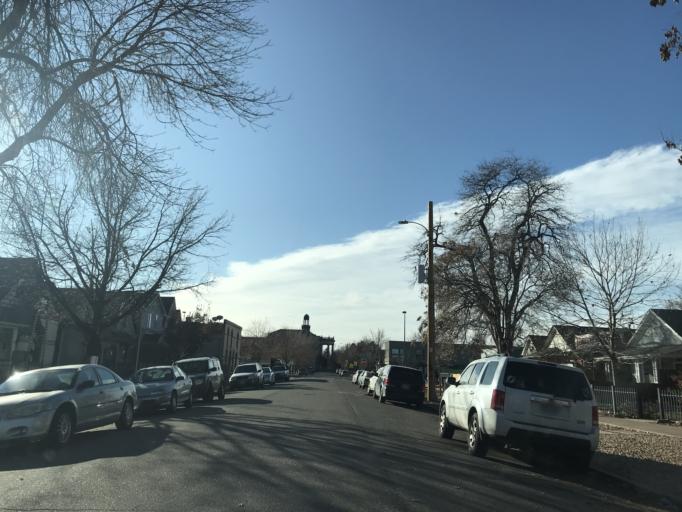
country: US
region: Colorado
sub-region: Denver County
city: Denver
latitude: 39.7655
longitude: -104.9697
